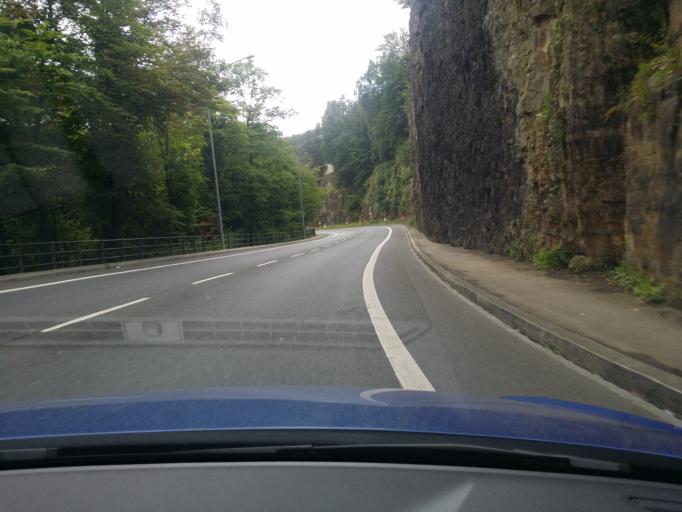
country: LU
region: Luxembourg
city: Kirchberg
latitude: 49.6084
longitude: 6.1459
